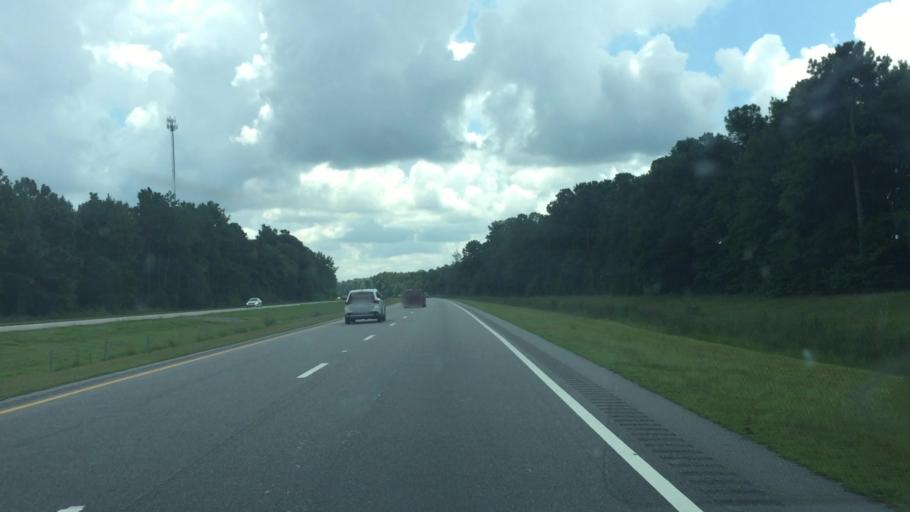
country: US
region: North Carolina
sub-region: Columbus County
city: Chadbourn
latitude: 34.4150
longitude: -78.9351
